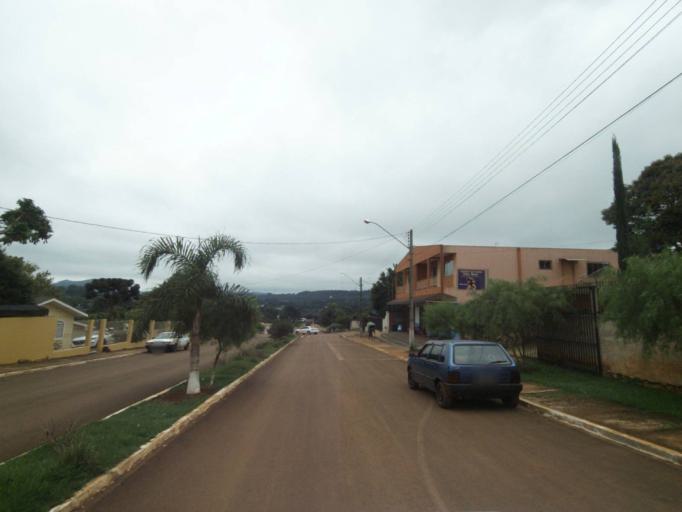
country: BR
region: Parana
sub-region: Pitanga
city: Pitanga
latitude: -24.9382
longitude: -51.8724
